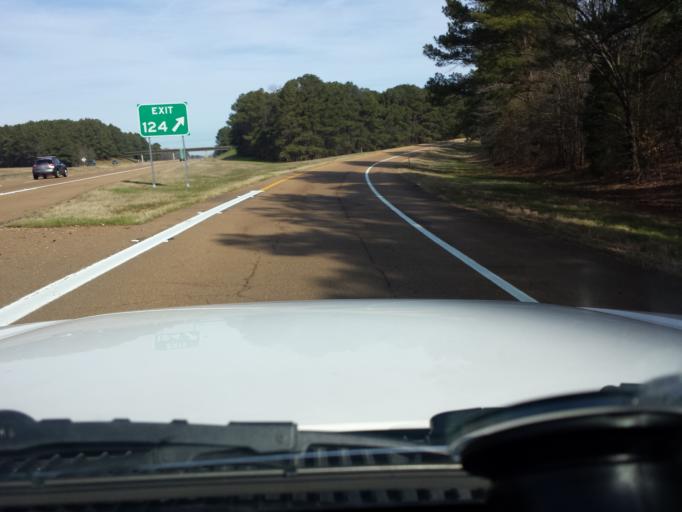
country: US
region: Mississippi
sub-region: Madison County
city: Canton
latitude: 32.6780
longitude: -90.0584
